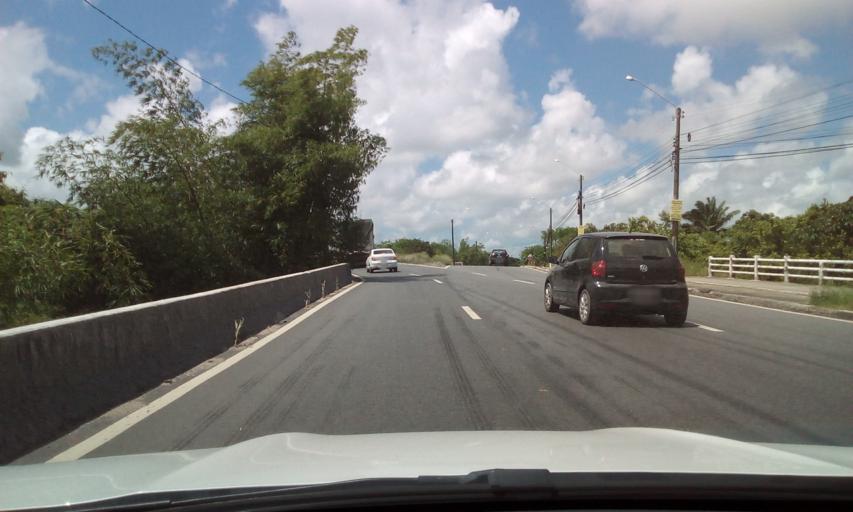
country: BR
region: Pernambuco
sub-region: Igarassu
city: Igarassu
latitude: -7.8351
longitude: -34.9125
